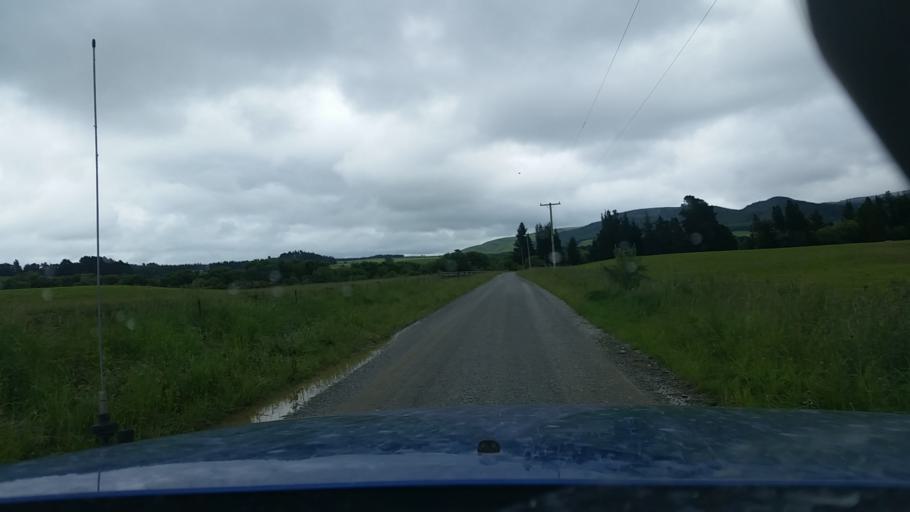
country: NZ
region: Canterbury
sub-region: Ashburton District
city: Methven
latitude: -43.6672
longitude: 171.4338
